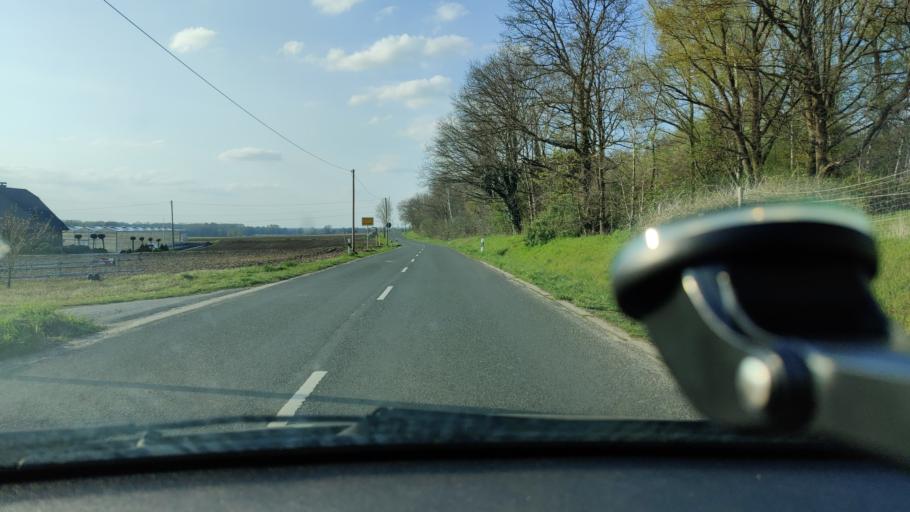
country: DE
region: North Rhine-Westphalia
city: Straelen
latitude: 51.3935
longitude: 6.2507
